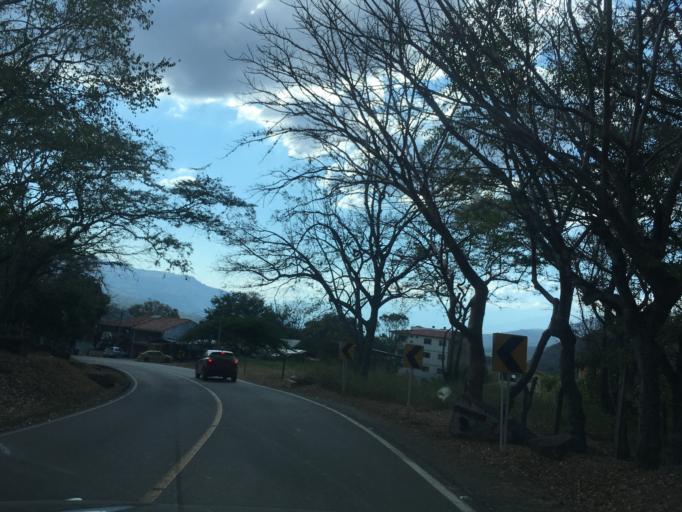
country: CO
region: Santander
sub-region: San Gil
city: San Gil
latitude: 6.5674
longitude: -73.1457
